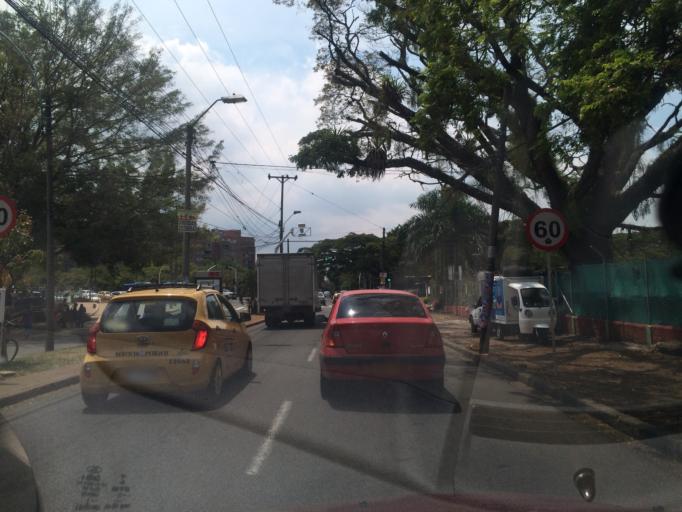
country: CO
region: Valle del Cauca
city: Cali
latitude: 3.3699
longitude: -76.5371
